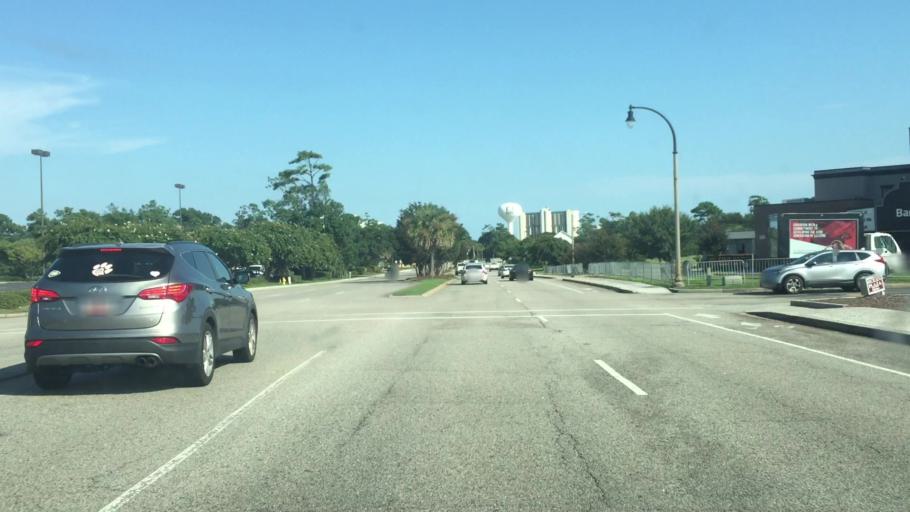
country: US
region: South Carolina
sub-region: Horry County
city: North Myrtle Beach
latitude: 33.8267
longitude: -78.6782
